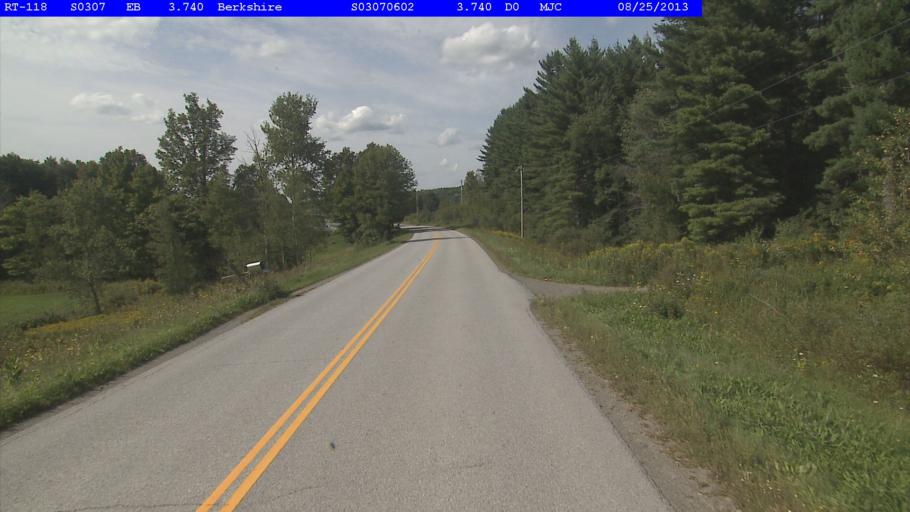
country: US
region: Vermont
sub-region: Franklin County
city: Enosburg Falls
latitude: 44.9689
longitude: -72.7622
